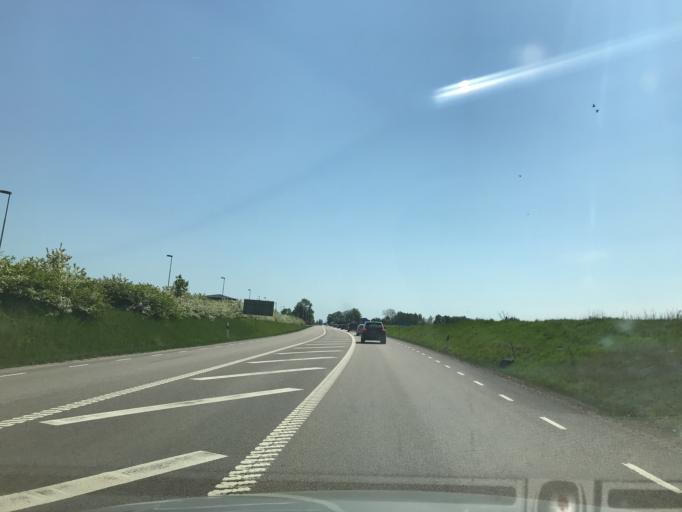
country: SE
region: Skane
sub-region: Astorps Kommun
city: Kvidinge
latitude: 56.1894
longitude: 13.0538
